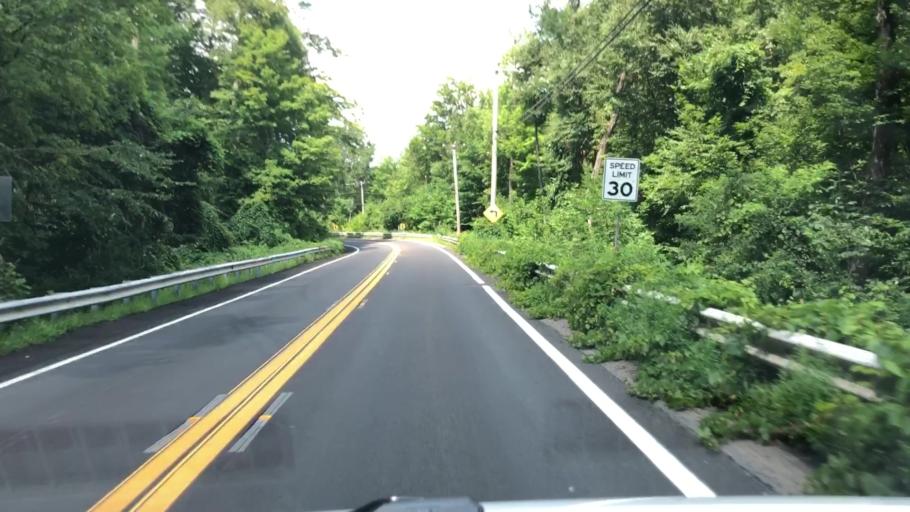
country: US
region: Massachusetts
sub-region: Franklin County
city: Ashfield
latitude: 42.5250
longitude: -72.7836
